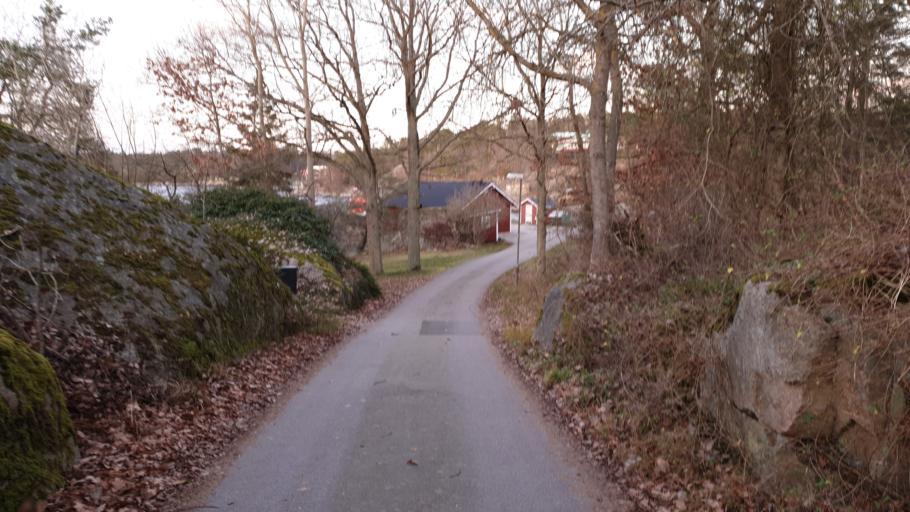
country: SE
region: Blekinge
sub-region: Karlshamns Kommun
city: Karlshamn
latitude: 56.1565
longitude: 14.8768
